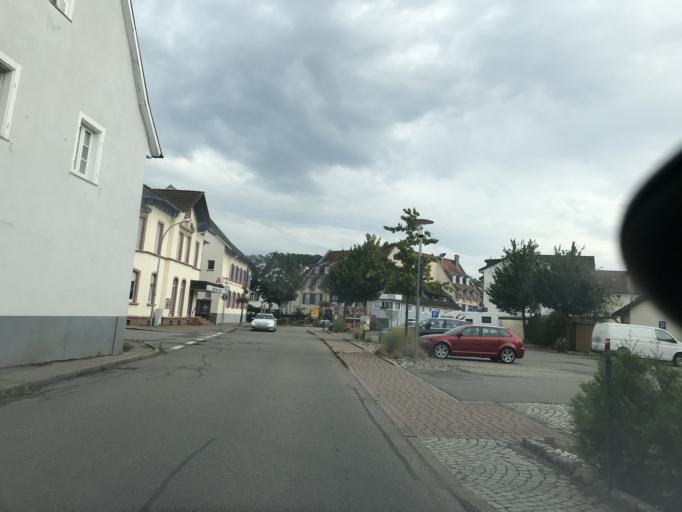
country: DE
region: Baden-Wuerttemberg
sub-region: Freiburg Region
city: Steinen
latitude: 47.6444
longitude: 7.7392
